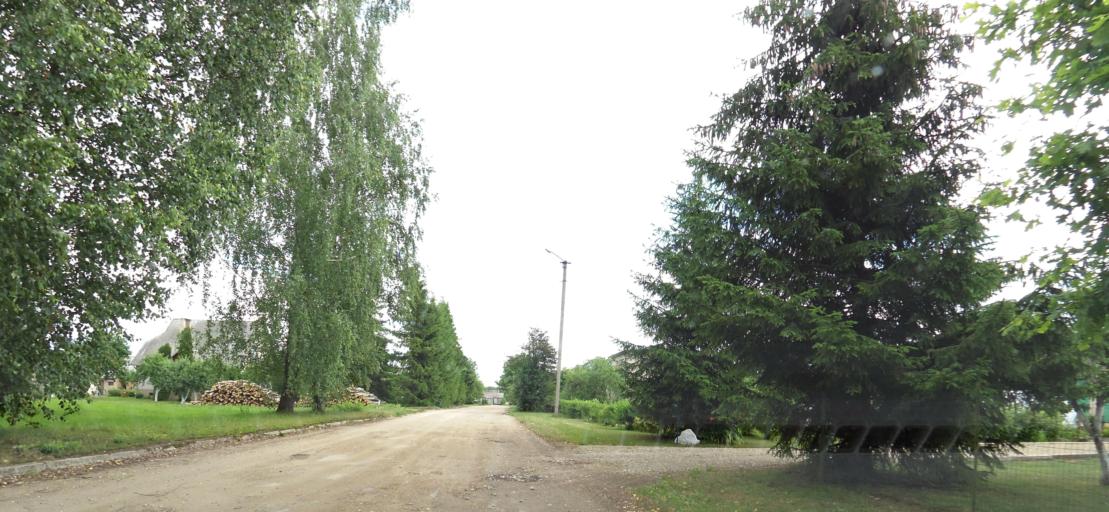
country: LT
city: Vabalninkas
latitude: 55.9077
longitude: 24.8069
